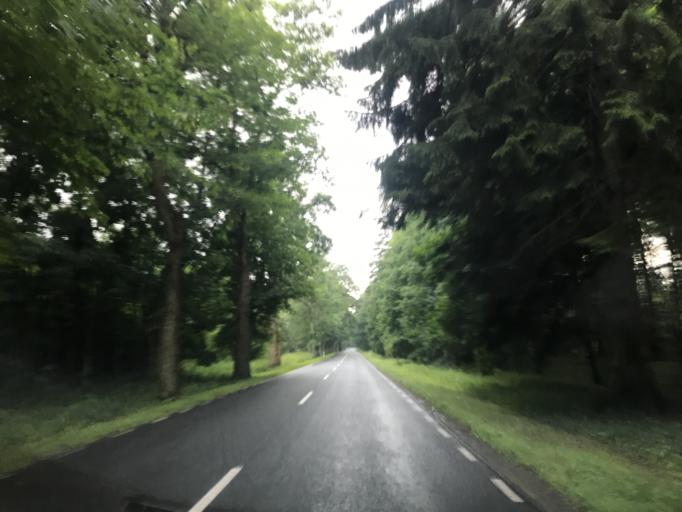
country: PL
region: West Pomeranian Voivodeship
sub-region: Powiat szczecinecki
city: Grzmiaca
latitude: 53.9760
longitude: 16.4316
